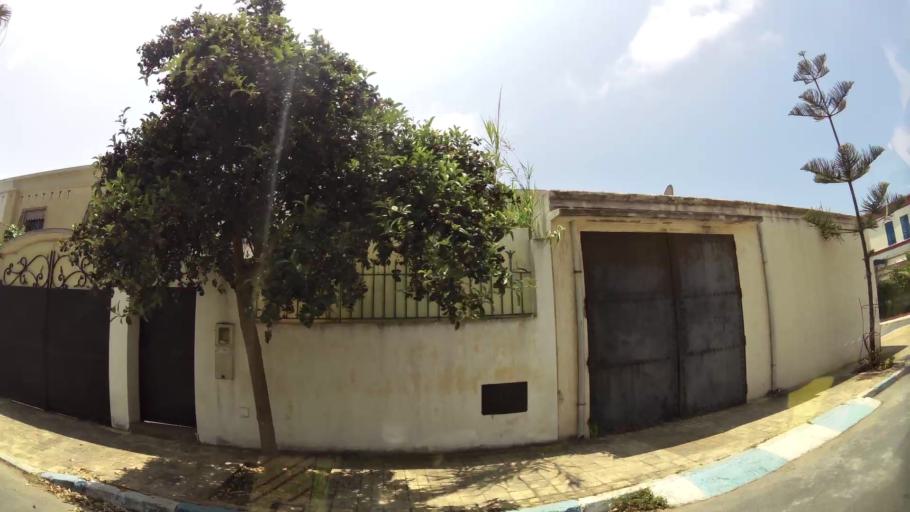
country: MA
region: Rabat-Sale-Zemmour-Zaer
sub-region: Skhirate-Temara
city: Temara
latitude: 33.9718
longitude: -6.9025
